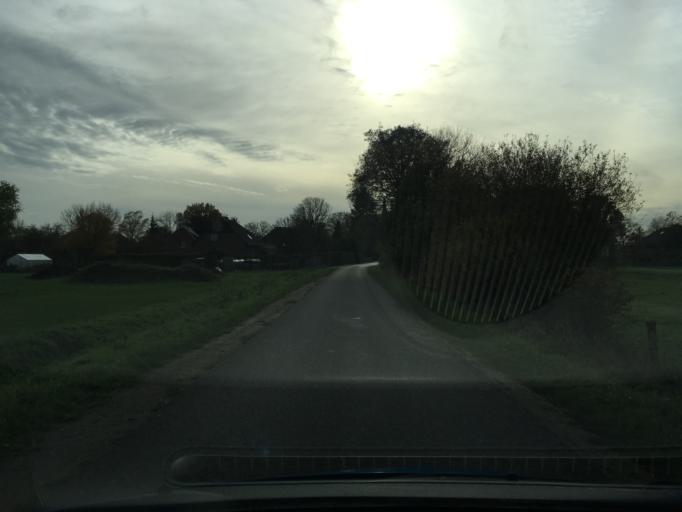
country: DE
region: Lower Saxony
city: Brietlingen
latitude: 53.3544
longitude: 10.4439
